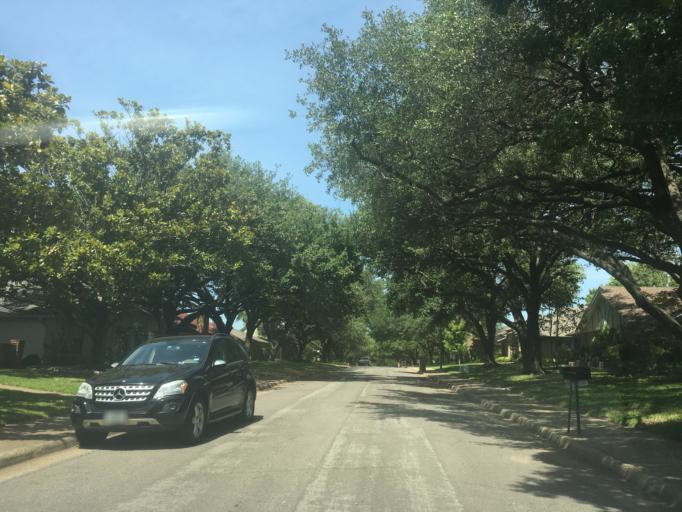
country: US
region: Texas
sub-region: Dallas County
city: Richardson
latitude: 32.8847
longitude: -96.7374
